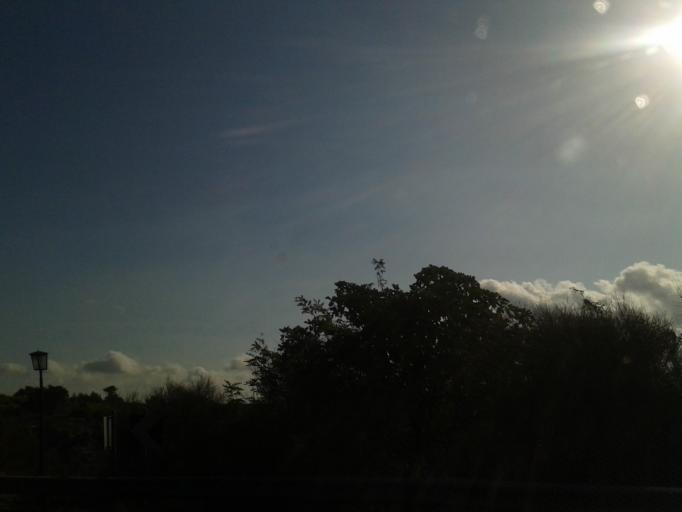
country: GR
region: Attica
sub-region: Nomarchia Anatolikis Attikis
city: Stamata
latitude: 38.1643
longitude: 23.9046
